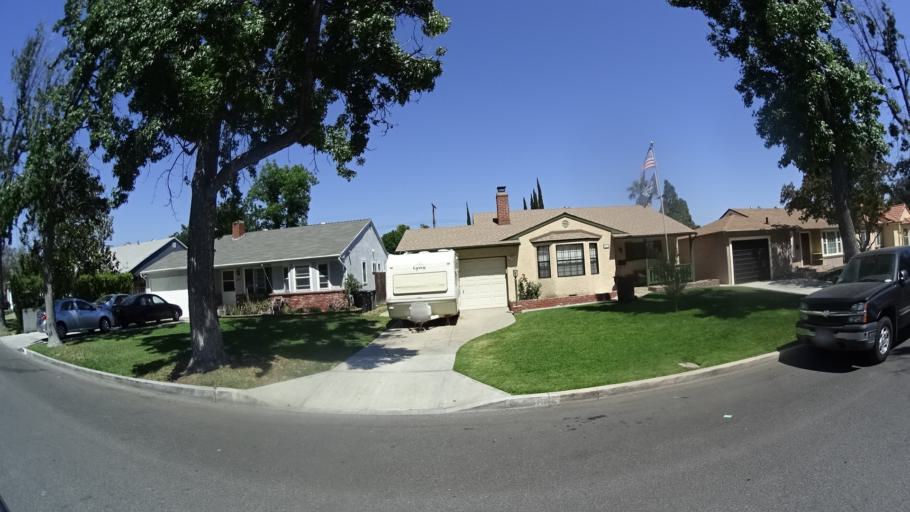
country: US
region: California
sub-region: Los Angeles County
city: North Hollywood
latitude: 34.1814
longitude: -118.3527
